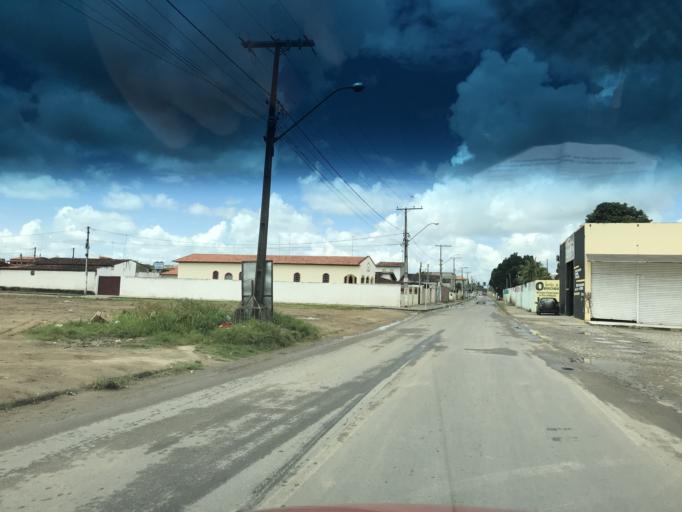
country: BR
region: Bahia
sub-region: Conceicao Do Almeida
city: Conceicao do Almeida
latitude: -12.7330
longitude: -39.1896
